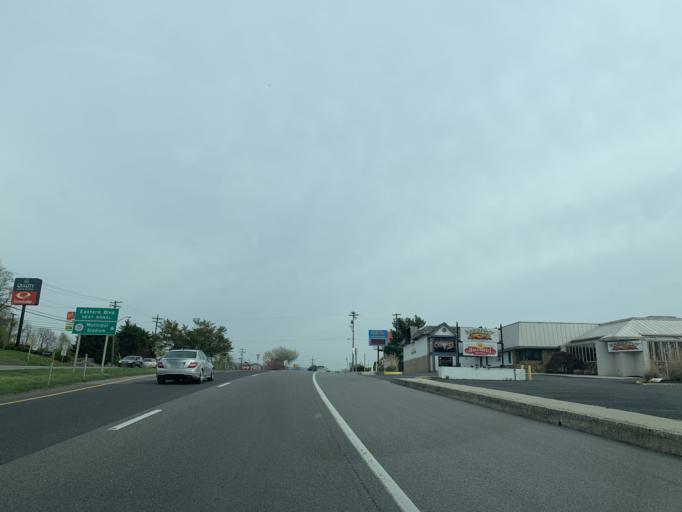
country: US
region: Maryland
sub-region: Washington County
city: Hagerstown
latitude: 39.6342
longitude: -77.7041
